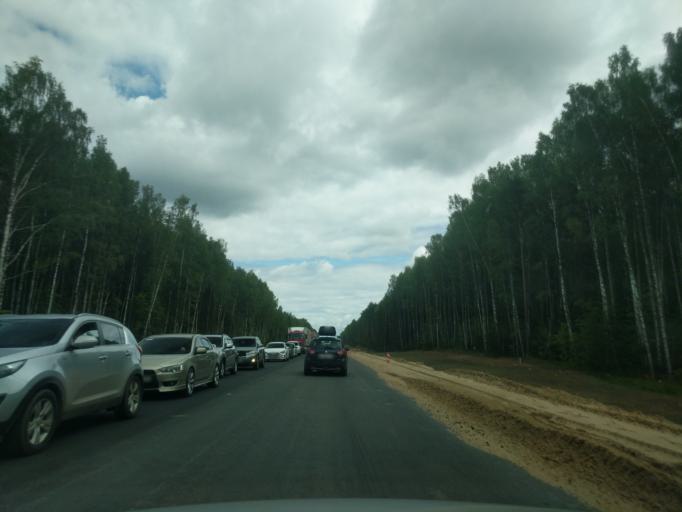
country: RU
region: Jaroslavl
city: Levashevo
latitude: 57.6888
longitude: 40.6181
